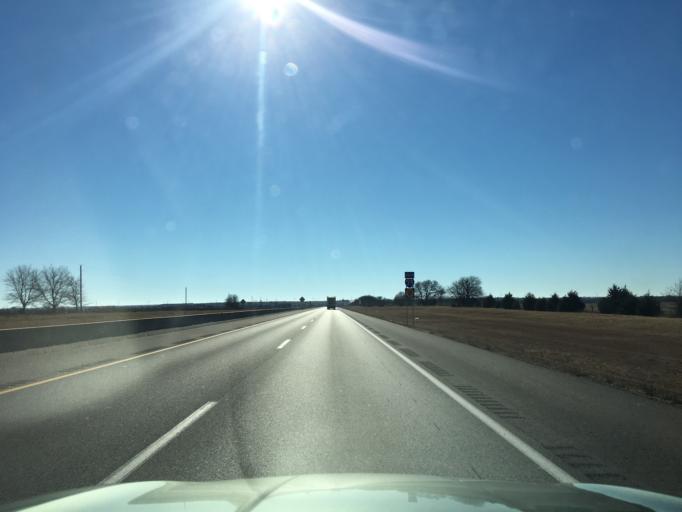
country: US
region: Kansas
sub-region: Sumner County
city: Wellington
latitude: 37.2322
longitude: -97.3389
